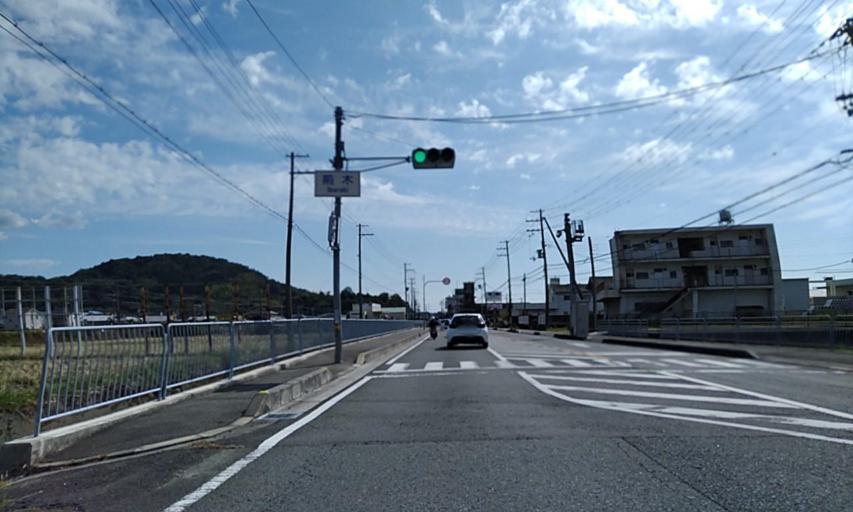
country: JP
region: Wakayama
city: Gobo
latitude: 33.9194
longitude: 135.1465
